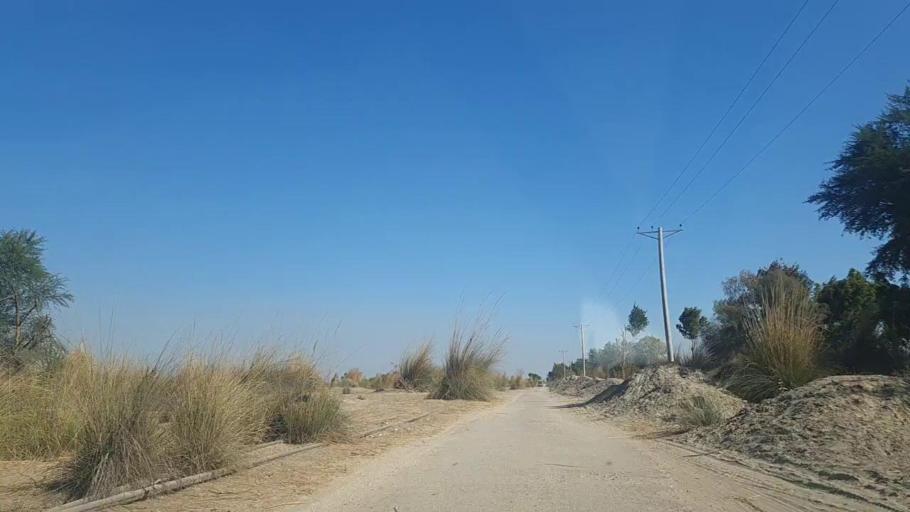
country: PK
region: Sindh
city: Khadro
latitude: 26.2093
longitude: 68.8715
